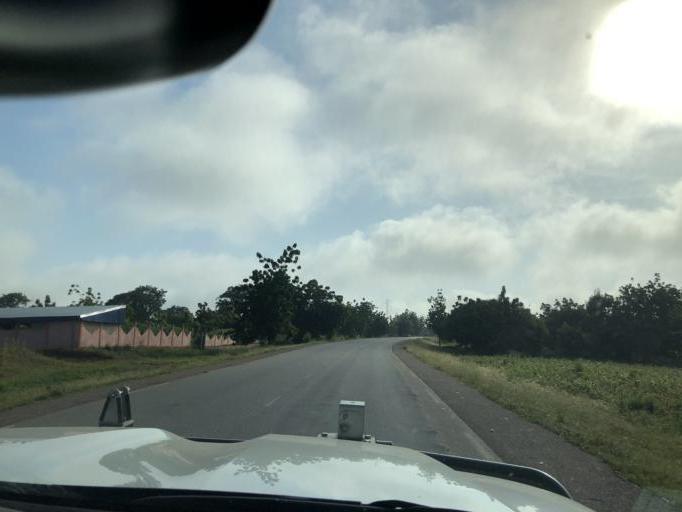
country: CM
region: North Province
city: Pitoa
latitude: 9.4940
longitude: 13.6889
